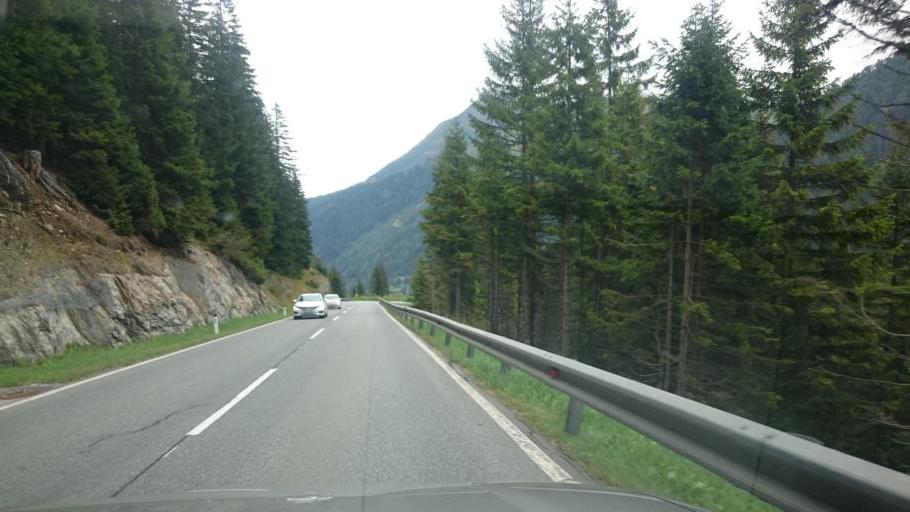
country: AT
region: Tyrol
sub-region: Politischer Bezirk Landeck
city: Sankt Anton am Arlberg
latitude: 47.1186
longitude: 10.2304
